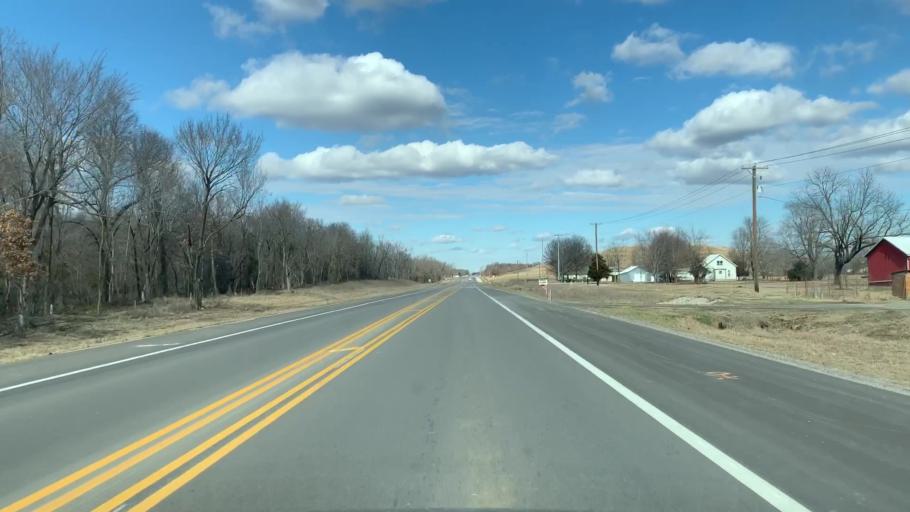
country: US
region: Kansas
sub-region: Cherokee County
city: Columbus
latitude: 37.2329
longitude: -94.8319
